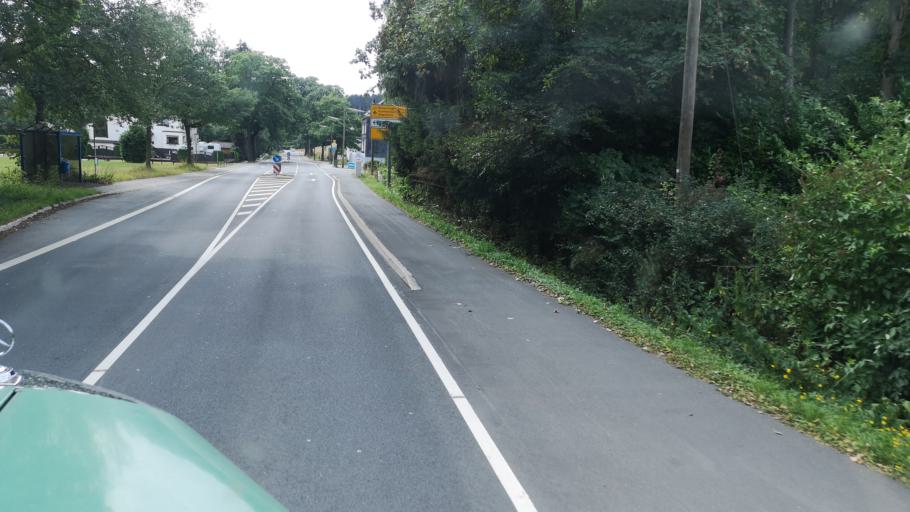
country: DE
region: North Rhine-Westphalia
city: Huckeswagen
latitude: 51.1379
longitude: 7.3454
